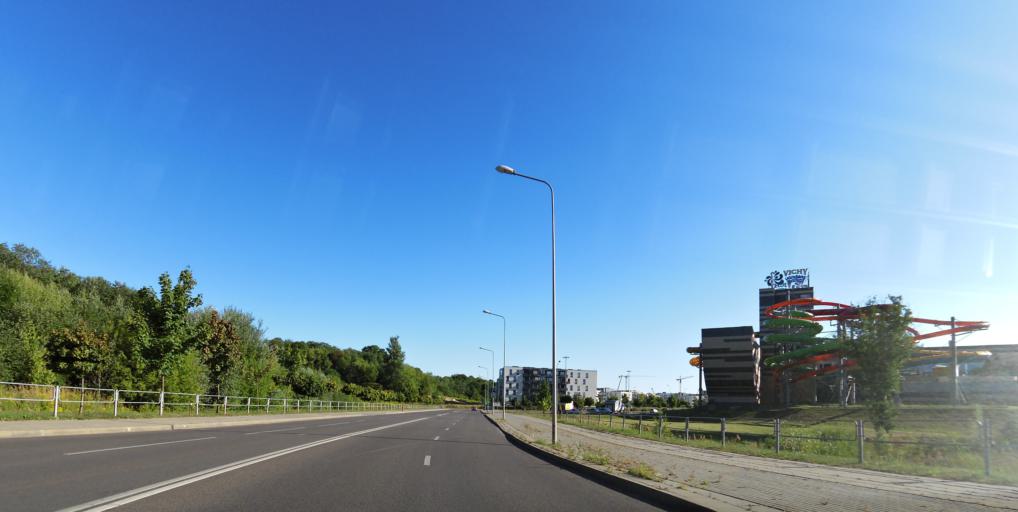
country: LT
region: Vilnius County
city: Seskine
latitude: 54.7157
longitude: 25.2745
